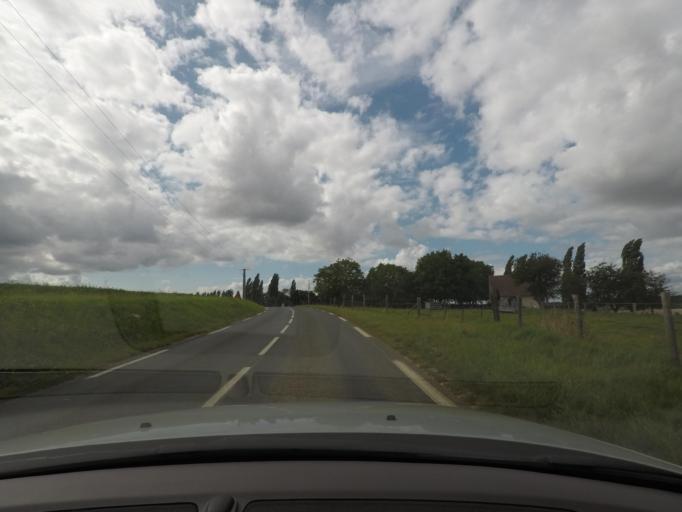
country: FR
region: Haute-Normandie
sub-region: Departement de l'Eure
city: Les Andelys
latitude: 49.2362
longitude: 1.4276
